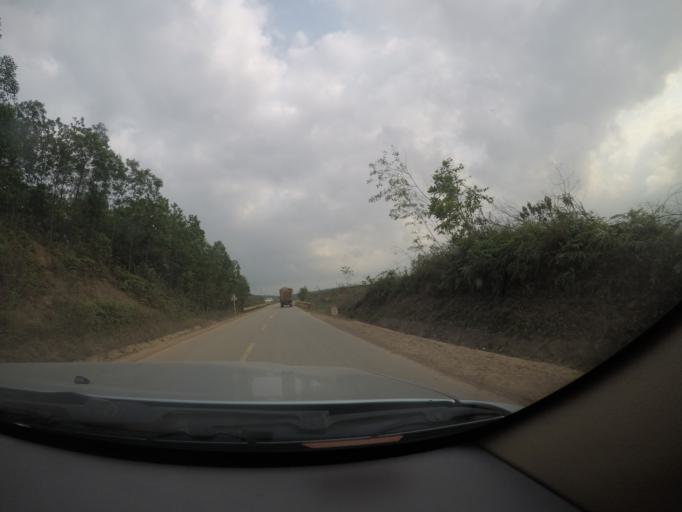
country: VN
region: Quang Tri
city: Ho Xa
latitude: 17.0851
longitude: 106.8605
